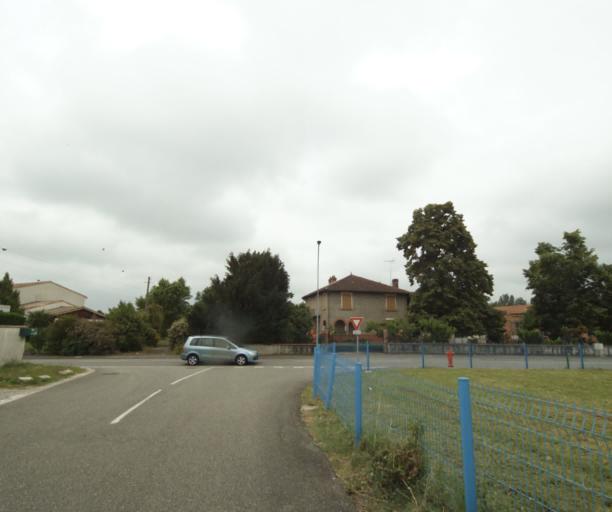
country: FR
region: Midi-Pyrenees
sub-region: Departement du Tarn-et-Garonne
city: Bressols
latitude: 43.9856
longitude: 1.3311
